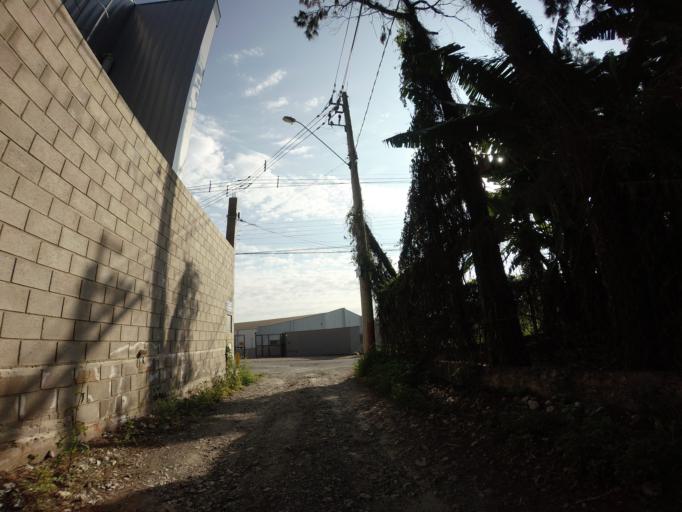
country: BR
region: Sao Paulo
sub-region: Piracicaba
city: Piracicaba
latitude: -22.7322
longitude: -47.5959
